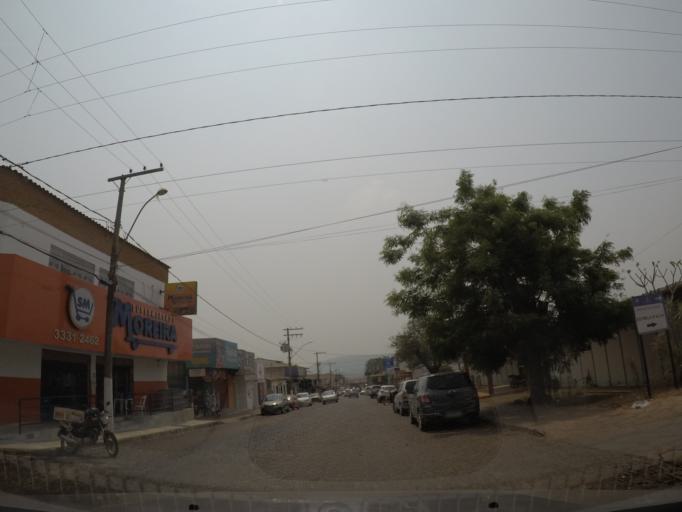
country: BR
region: Goias
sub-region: Pirenopolis
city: Pirenopolis
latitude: -15.8575
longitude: -48.9581
